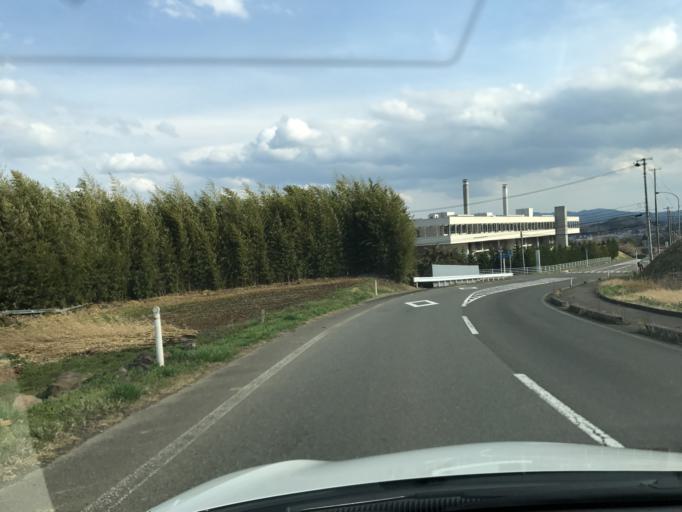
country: JP
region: Miyagi
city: Shiroishi
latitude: 38.0135
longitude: 140.6082
